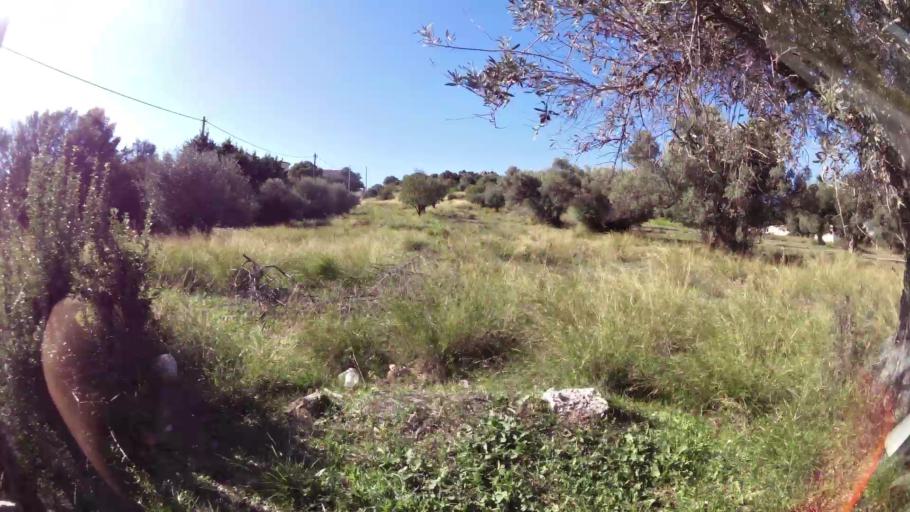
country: GR
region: Attica
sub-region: Nomarchia Anatolikis Attikis
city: Paiania
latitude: 37.9707
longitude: 23.8625
